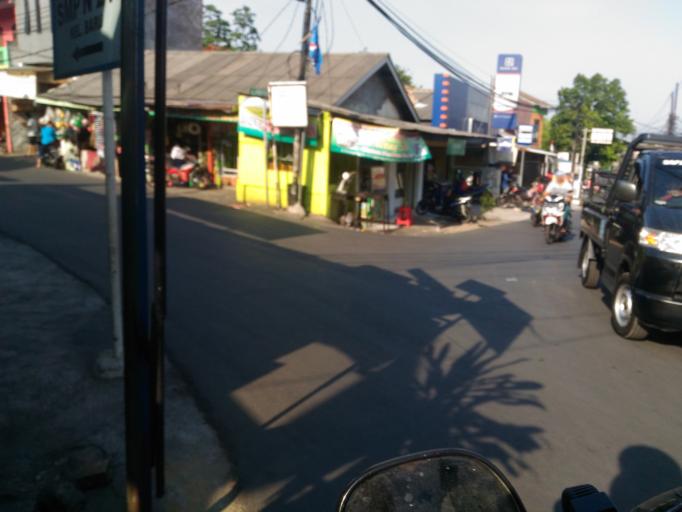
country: ID
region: West Java
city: Depok
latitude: -6.3266
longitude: 106.8559
